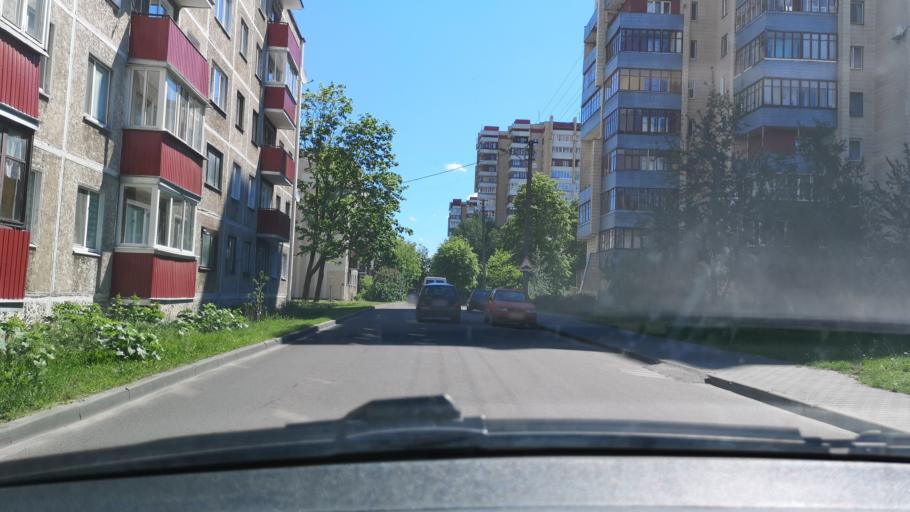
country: BY
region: Brest
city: Brest
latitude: 52.0836
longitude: 23.6893
